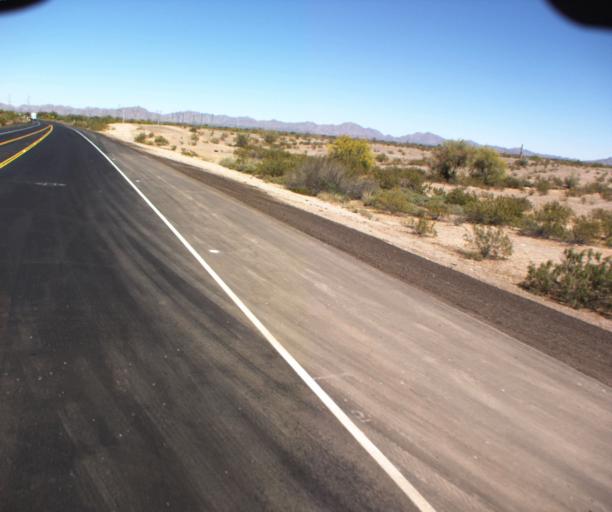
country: US
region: Arizona
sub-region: Maricopa County
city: Gila Bend
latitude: 32.9625
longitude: -112.6781
